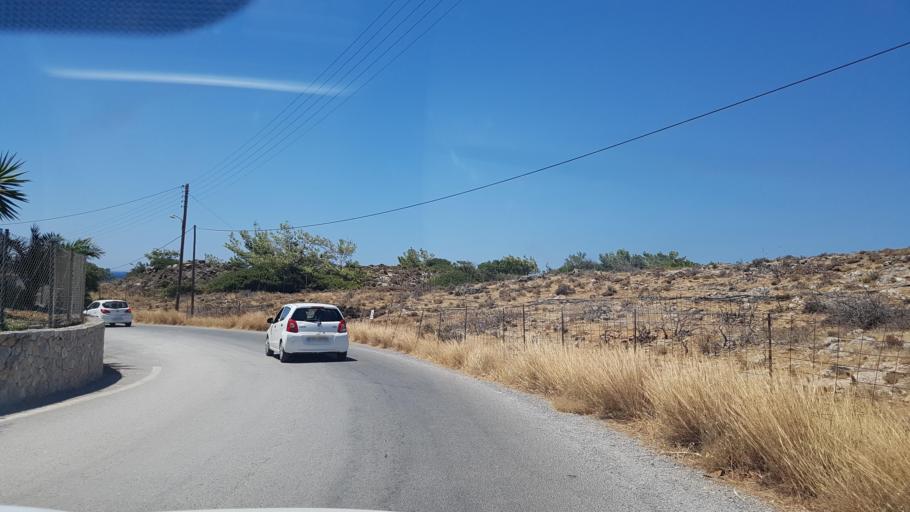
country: GR
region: Crete
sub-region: Nomos Chanias
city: Palaiochora
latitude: 35.2765
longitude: 23.5448
